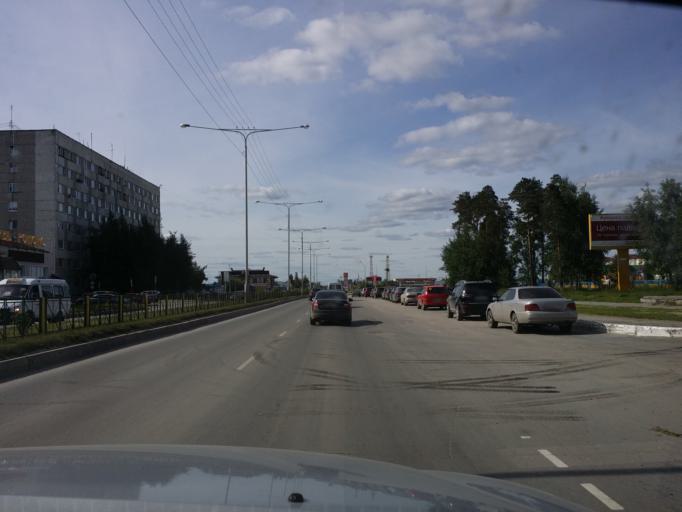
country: RU
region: Khanty-Mansiyskiy Avtonomnyy Okrug
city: Nizhnevartovsk
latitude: 60.9489
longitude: 76.5643
